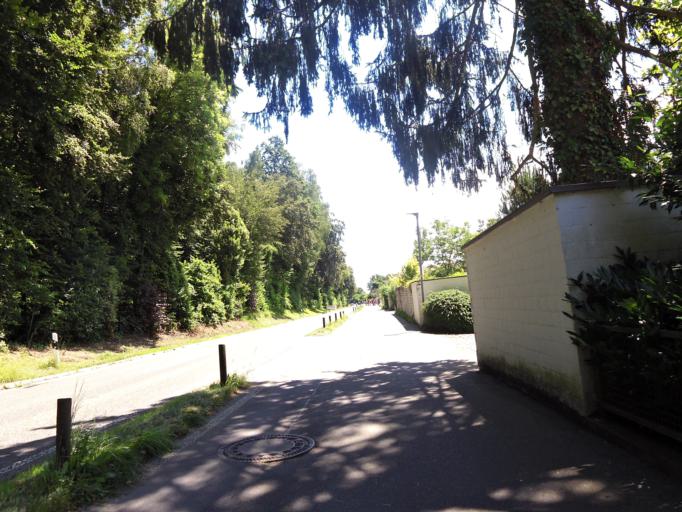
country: DE
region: Baden-Wuerttemberg
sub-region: Tuebingen Region
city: Uhldingen-Muhlhofen
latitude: 47.7102
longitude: 9.2414
